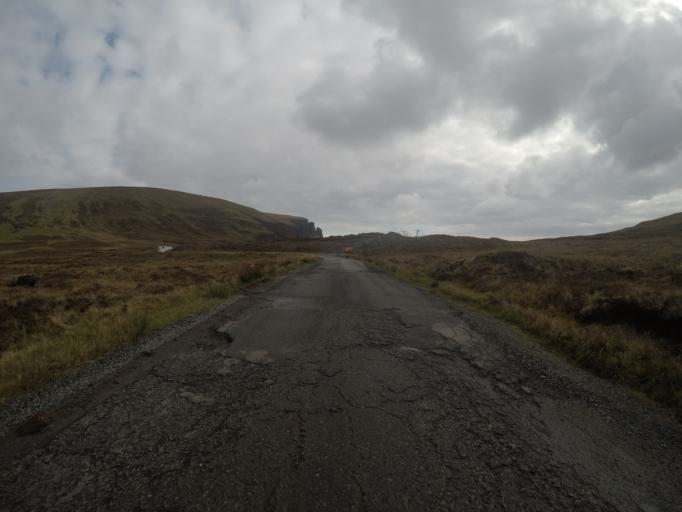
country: GB
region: Scotland
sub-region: Highland
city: Portree
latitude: 57.6261
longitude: -6.2947
